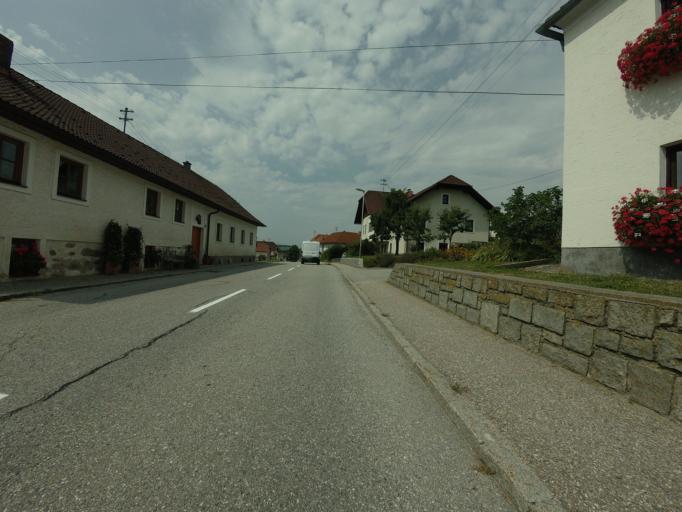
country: AT
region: Upper Austria
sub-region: Politischer Bezirk Urfahr-Umgebung
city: Reichenthal
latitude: 48.5505
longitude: 14.4439
